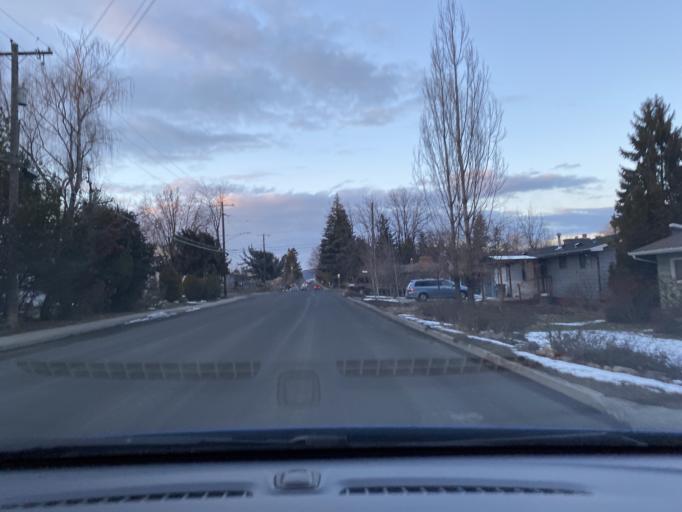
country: US
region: Idaho
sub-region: Latah County
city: Moscow
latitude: 46.7418
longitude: -116.9854
